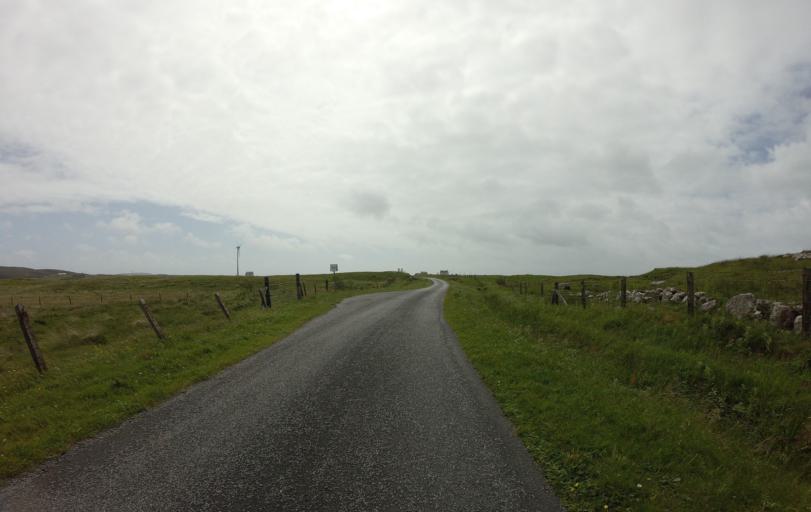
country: GB
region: Scotland
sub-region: Eilean Siar
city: Isle of South Uist
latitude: 57.2452
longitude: -7.4049
